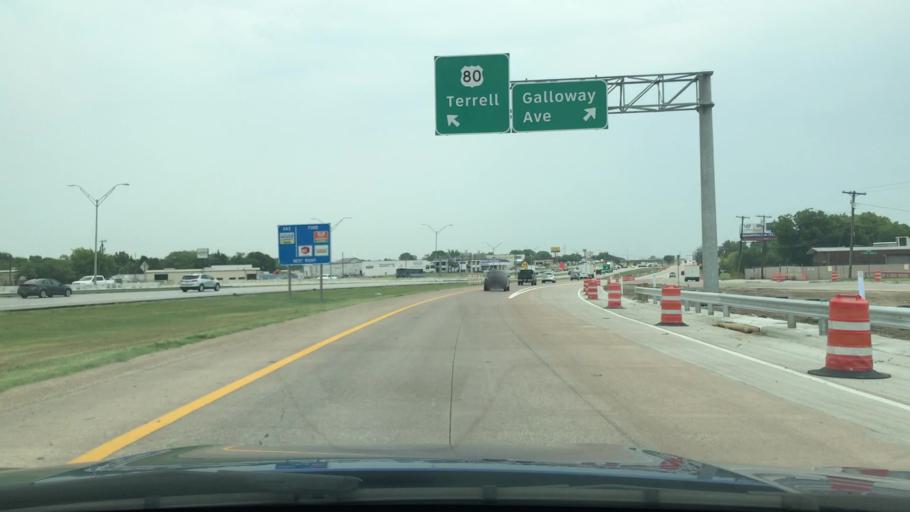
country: US
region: Texas
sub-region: Dallas County
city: Mesquite
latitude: 32.7922
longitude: -96.6218
